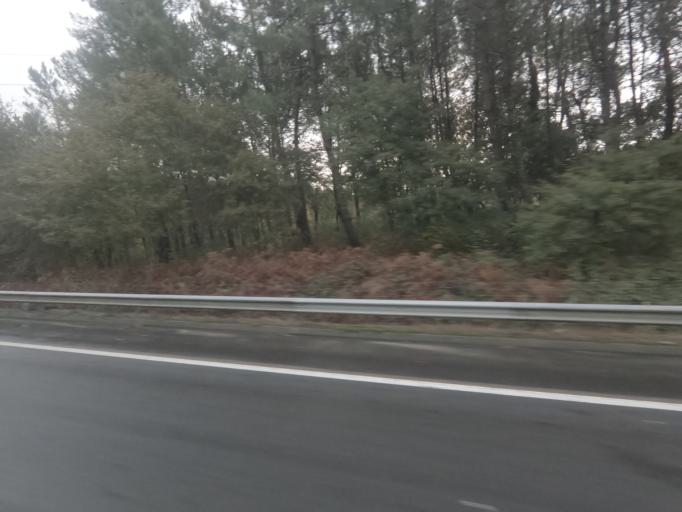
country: ES
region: Galicia
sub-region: Provincia de Pontevedra
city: Porrino
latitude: 42.2162
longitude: -8.6546
